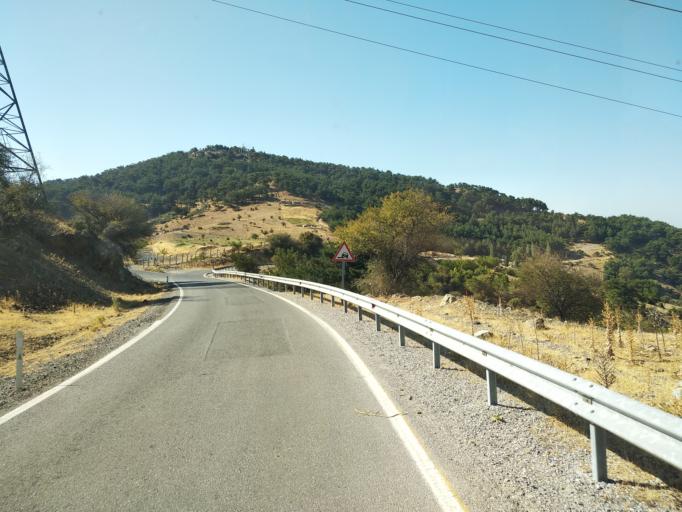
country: TR
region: Izmir
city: Gaziemir
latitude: 38.3257
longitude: 27.0045
